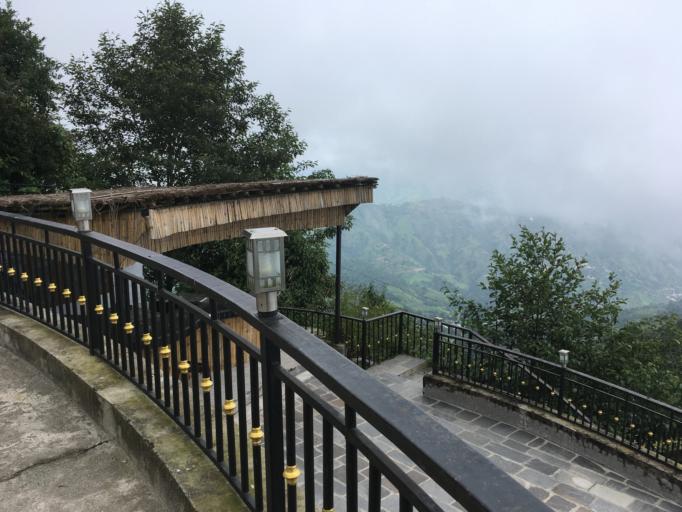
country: NP
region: Central Region
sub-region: Bagmati Zone
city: Nagarkot
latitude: 27.7280
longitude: 85.5259
